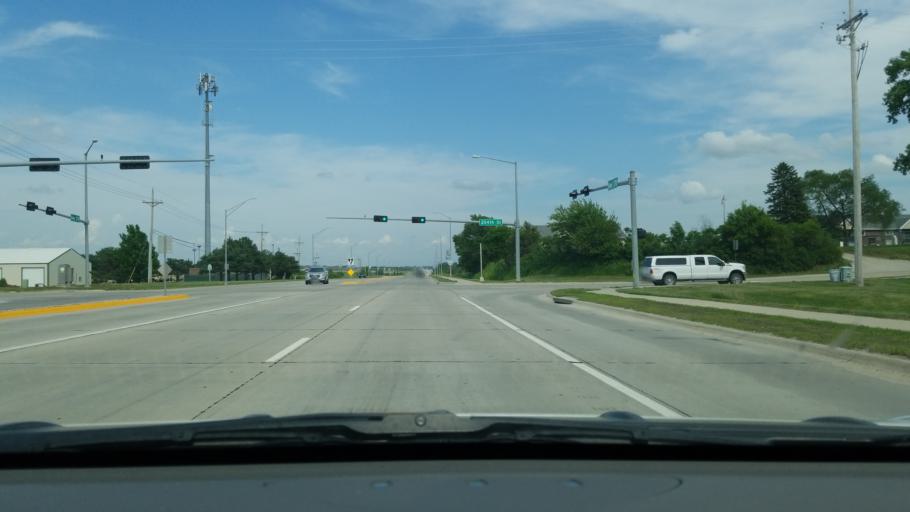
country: US
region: Nebraska
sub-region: Sarpy County
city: Gretna
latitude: 41.1469
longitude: -96.2349
